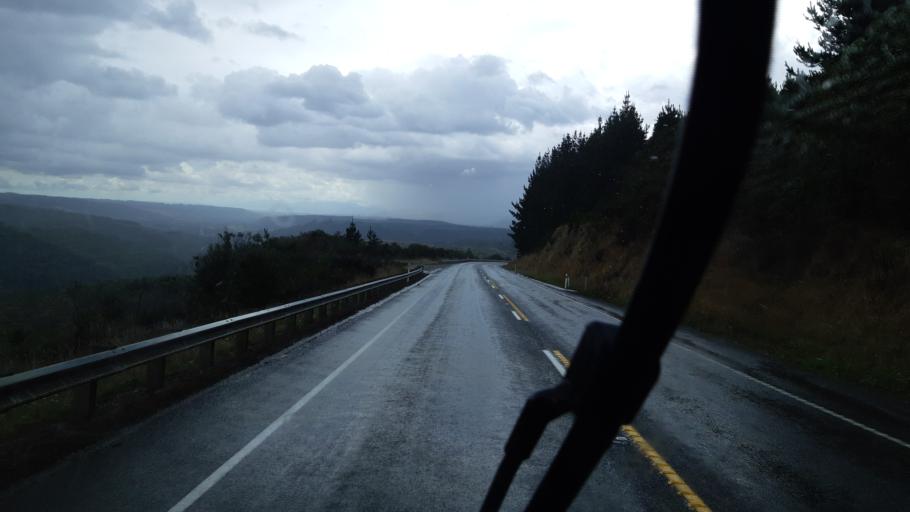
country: NZ
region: Tasman
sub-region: Tasman District
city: Wakefield
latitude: -41.4798
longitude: 172.9173
